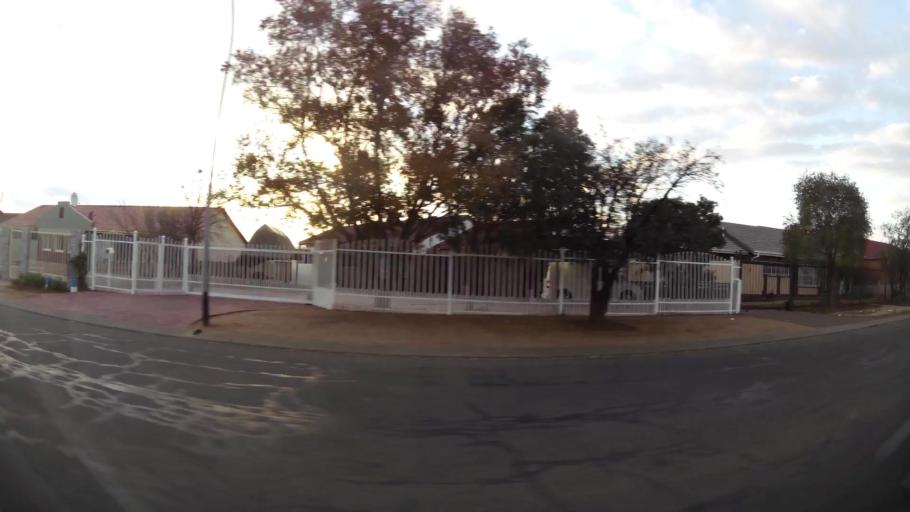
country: ZA
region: Orange Free State
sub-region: Mangaung Metropolitan Municipality
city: Bloemfontein
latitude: -29.1610
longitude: 26.1874
